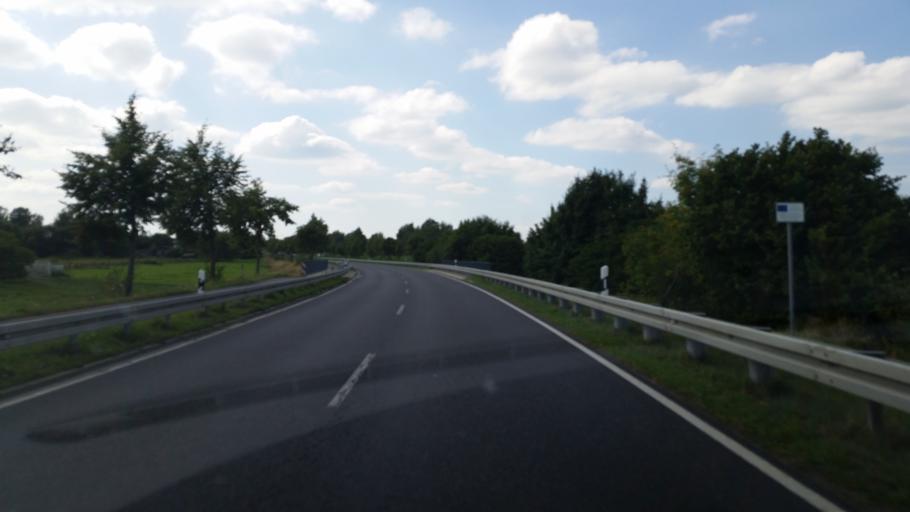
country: DE
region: Saxony
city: Kamenz
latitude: 51.2868
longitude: 14.1266
